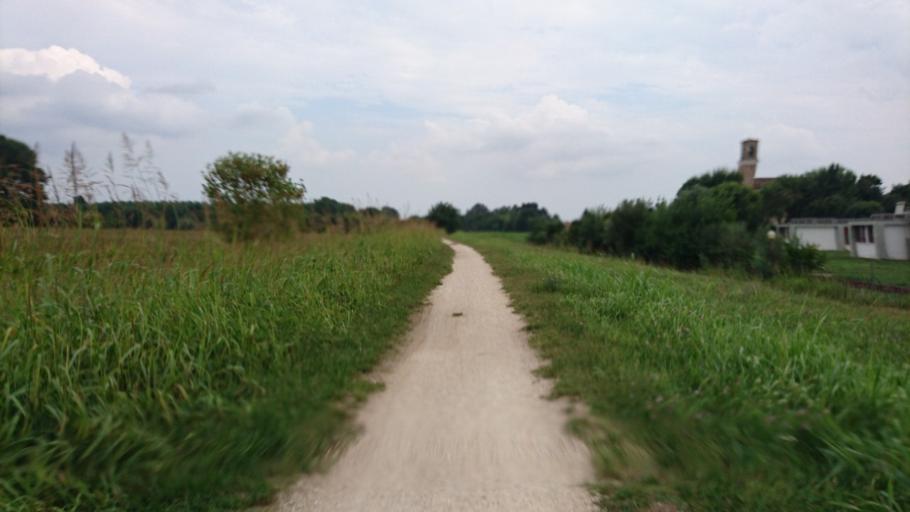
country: IT
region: Veneto
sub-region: Provincia di Padova
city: Saccolongo
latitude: 45.4063
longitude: 11.7463
